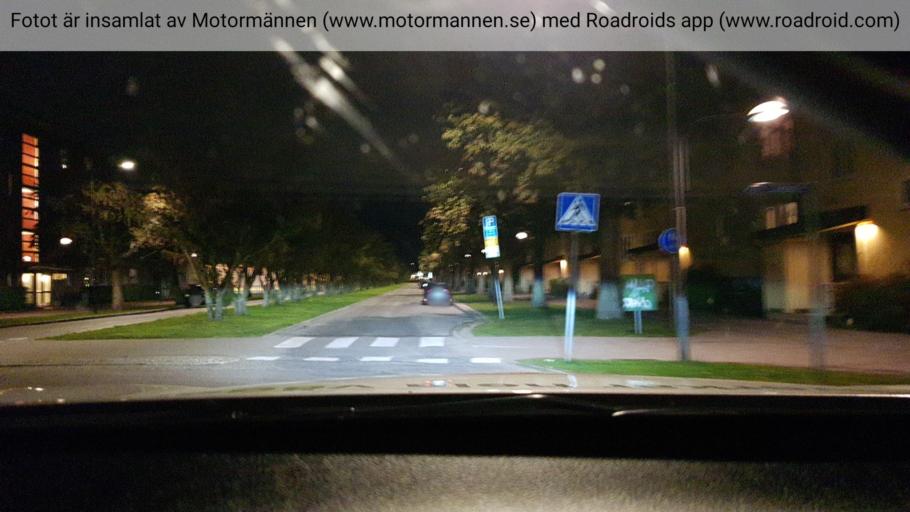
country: SE
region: Stockholm
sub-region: Stockholms Kommun
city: Arsta
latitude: 59.2818
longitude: 18.0783
